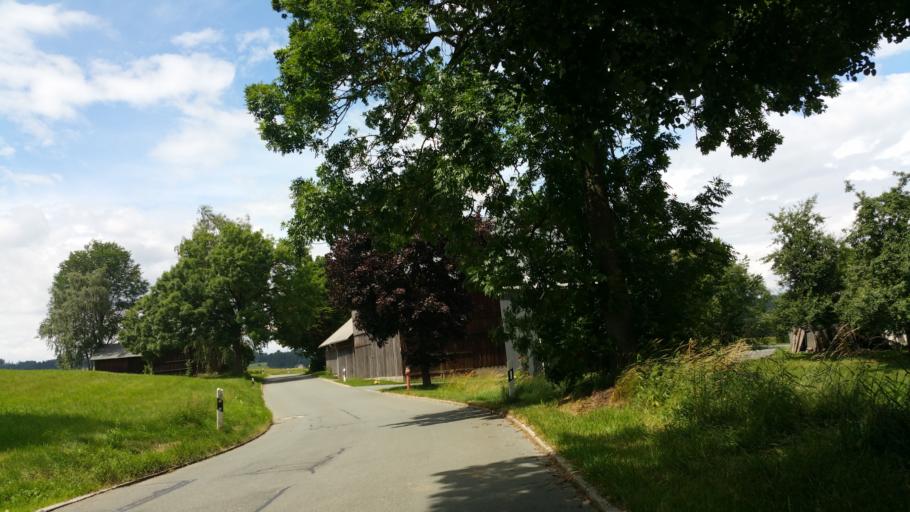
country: DE
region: Bavaria
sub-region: Upper Franconia
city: Schwarzenbach an der Saale
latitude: 50.2408
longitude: 11.9025
